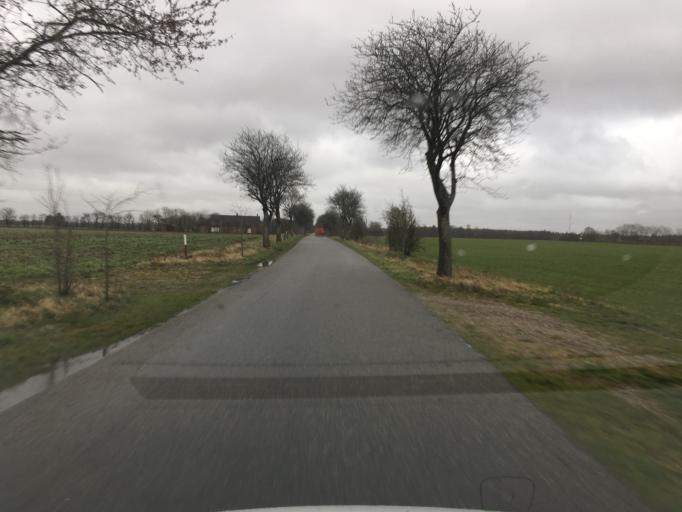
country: DK
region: South Denmark
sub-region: Aabenraa Kommune
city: Tinglev
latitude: 54.9023
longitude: 9.3014
